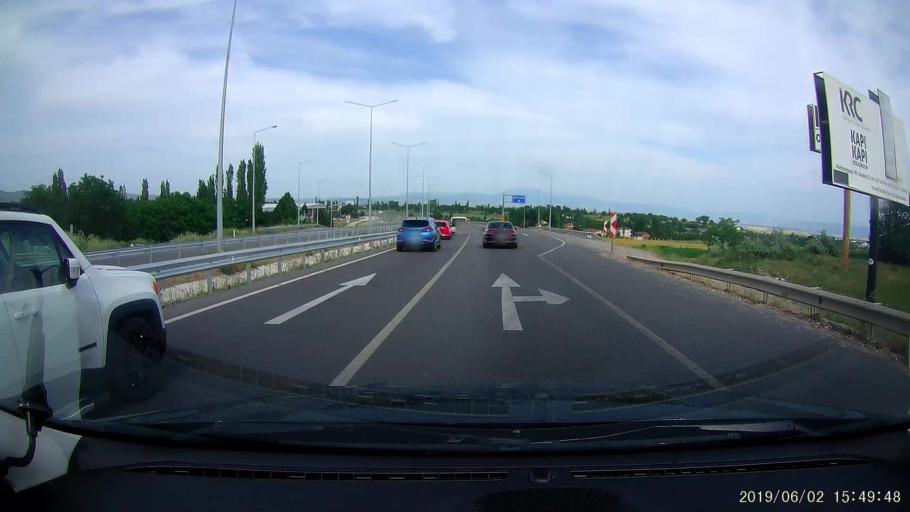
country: TR
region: Amasya
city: Merzifon
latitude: 40.8570
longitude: 35.4689
